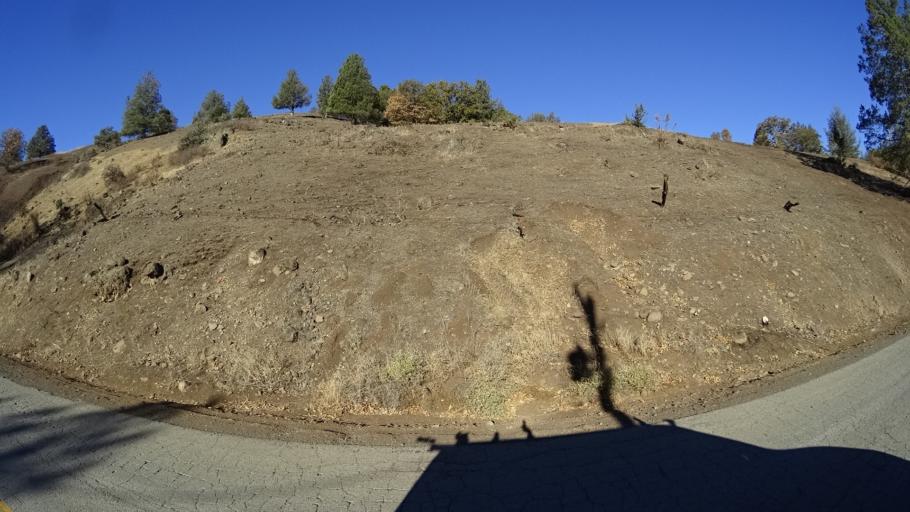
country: US
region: California
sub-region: Siskiyou County
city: Montague
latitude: 41.9219
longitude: -122.4498
